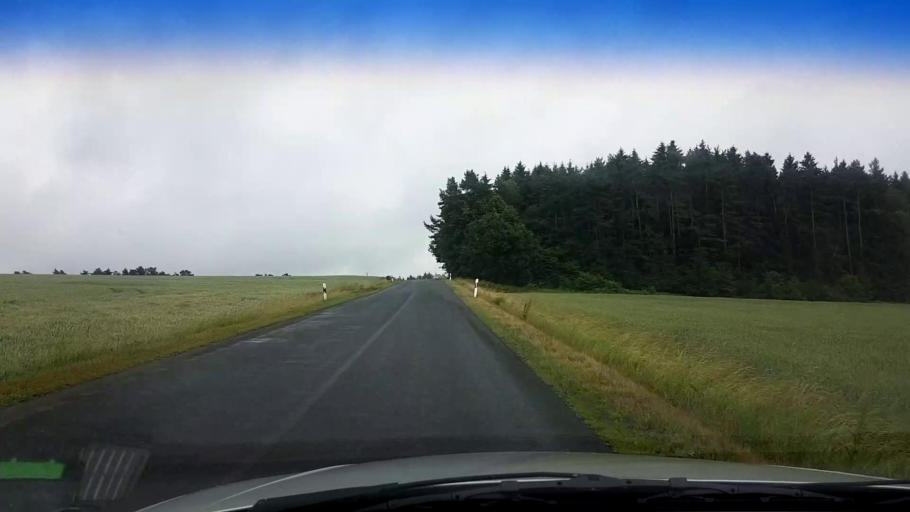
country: DE
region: Bavaria
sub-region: Upper Franconia
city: Wattendorf
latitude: 50.0534
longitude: 11.1232
